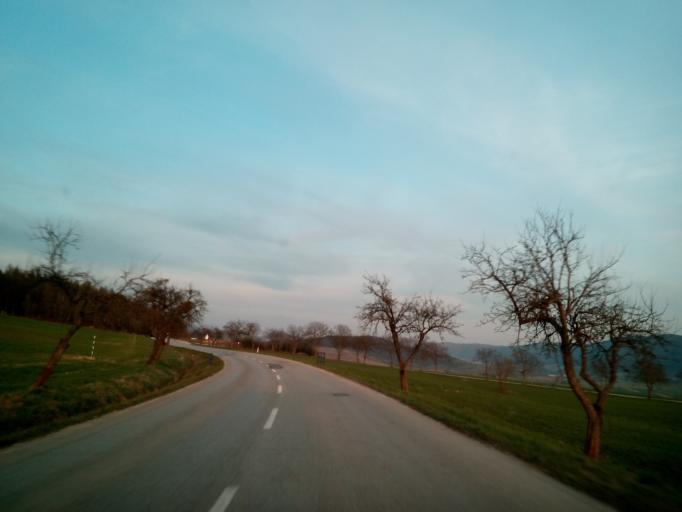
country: SK
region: Kosicky
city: Roznava
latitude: 48.6599
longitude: 20.4678
